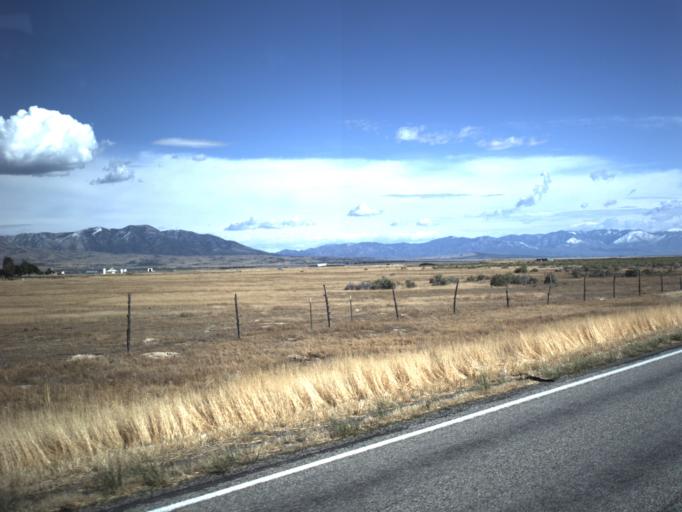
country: US
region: Utah
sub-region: Millard County
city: Delta
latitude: 39.3325
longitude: -112.4881
